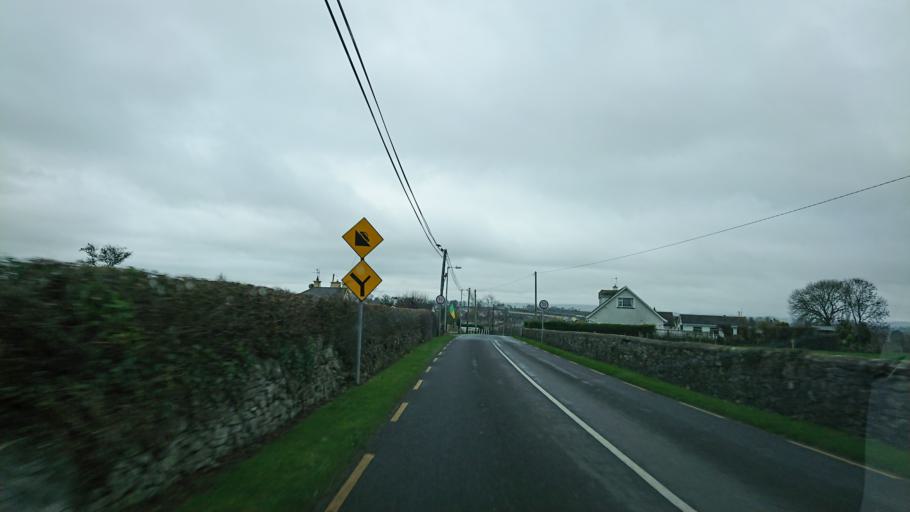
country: IE
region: Leinster
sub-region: Kilkenny
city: Kilkenny
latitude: 52.5457
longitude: -7.2722
